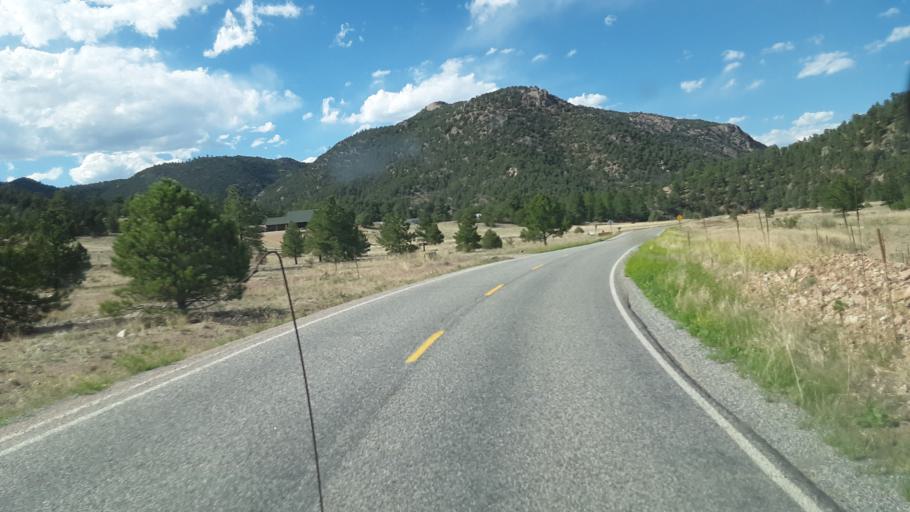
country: US
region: Colorado
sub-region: Fremont County
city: Canon City
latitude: 38.3832
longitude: -105.4564
